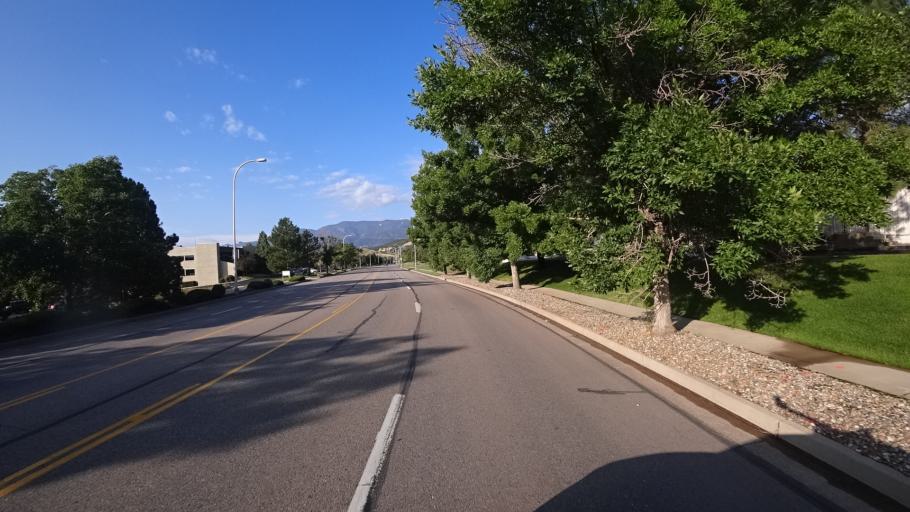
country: US
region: Colorado
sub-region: El Paso County
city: Manitou Springs
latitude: 38.9033
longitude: -104.8666
